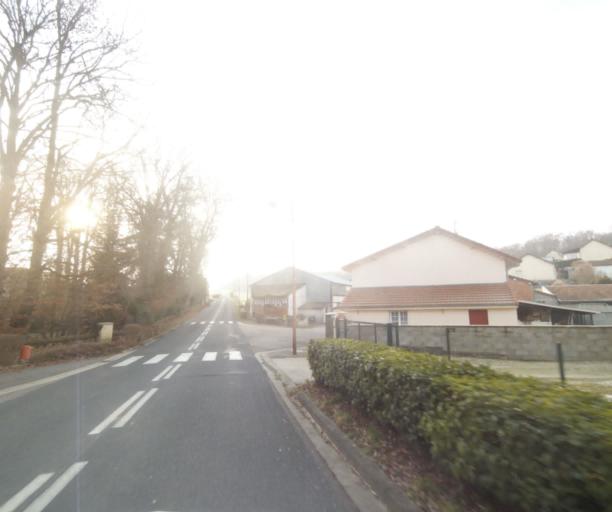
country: FR
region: Champagne-Ardenne
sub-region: Departement de la Haute-Marne
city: Chancenay
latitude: 48.7223
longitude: 4.9416
